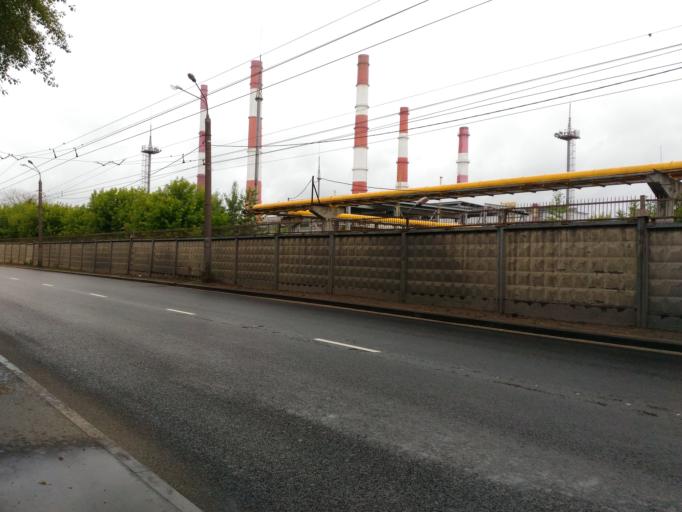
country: RU
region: Nizjnij Novgorod
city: Nizhniy Novgorod
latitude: 56.2425
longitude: 43.9003
